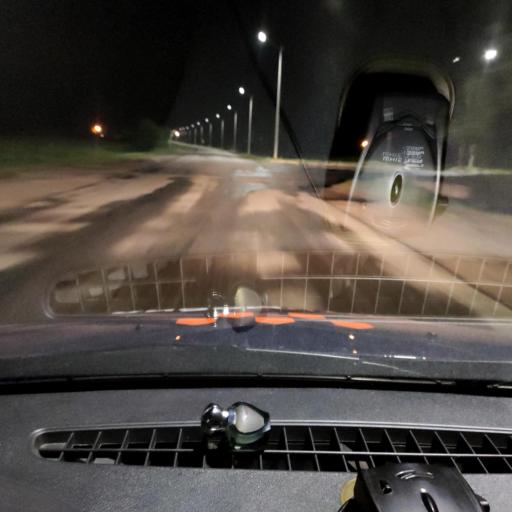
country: RU
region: Voronezj
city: Khrenovoye
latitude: 51.1163
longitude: 40.2641
